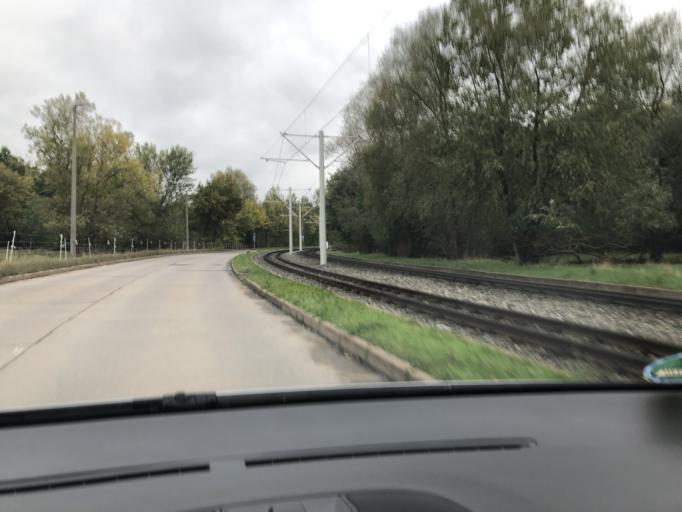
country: DE
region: Thuringia
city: Gera
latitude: 50.9060
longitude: 12.0769
